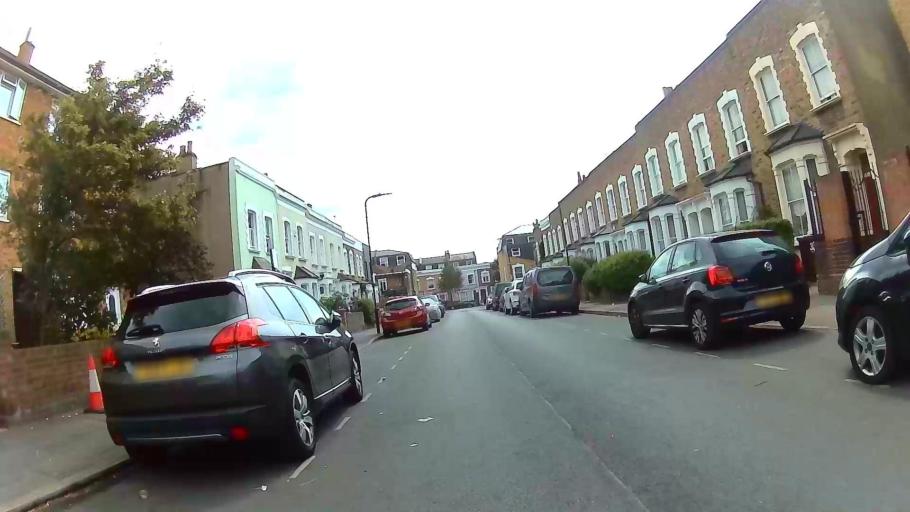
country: GB
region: England
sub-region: Greater London
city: Harringay
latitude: 51.5610
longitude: -0.0789
